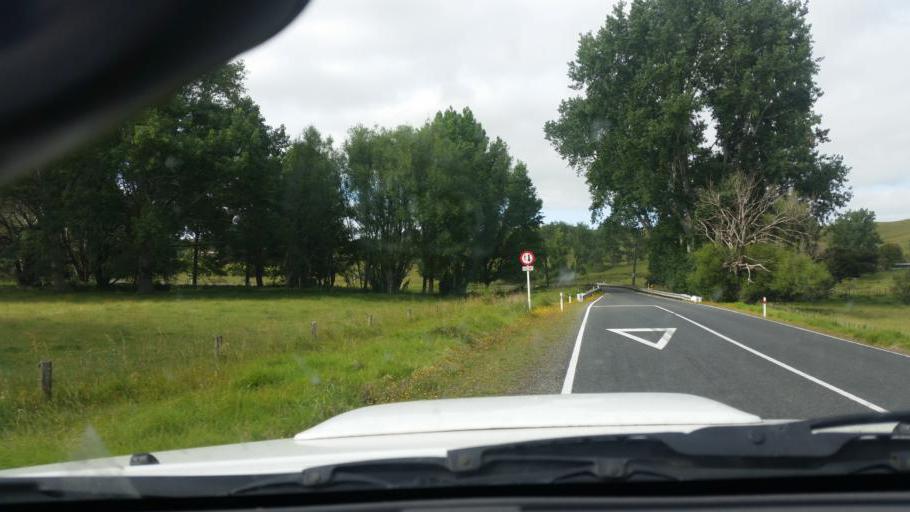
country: NZ
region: Northland
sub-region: Kaipara District
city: Dargaville
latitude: -35.8407
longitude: 173.8439
